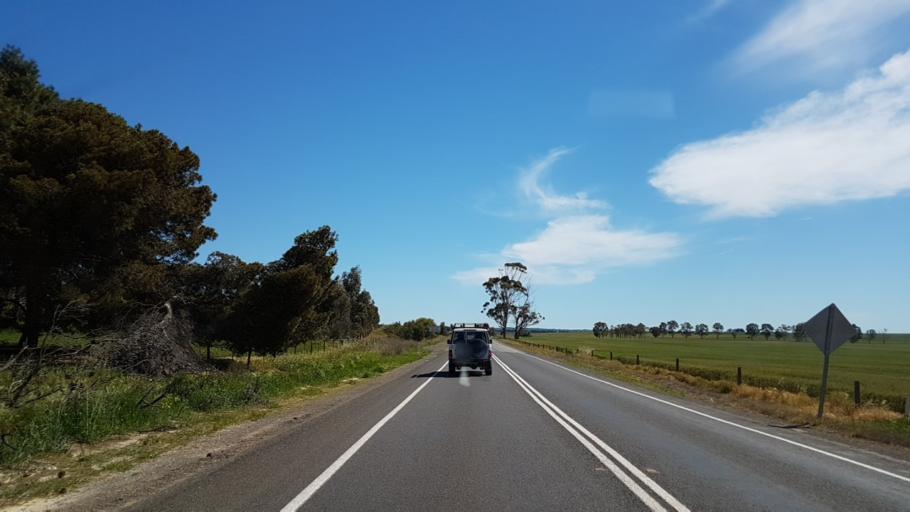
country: AU
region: South Australia
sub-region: Light
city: Kapunda
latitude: -34.2667
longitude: 138.7615
